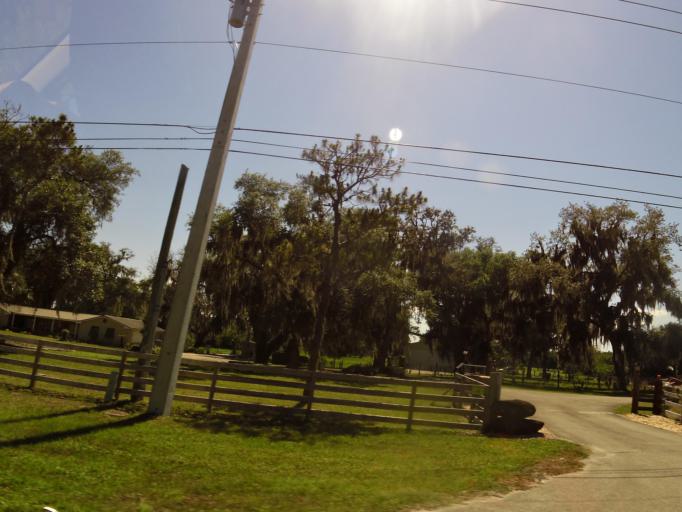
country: US
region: Florida
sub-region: Flagler County
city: Flagler Beach
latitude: 29.4271
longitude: -81.1521
